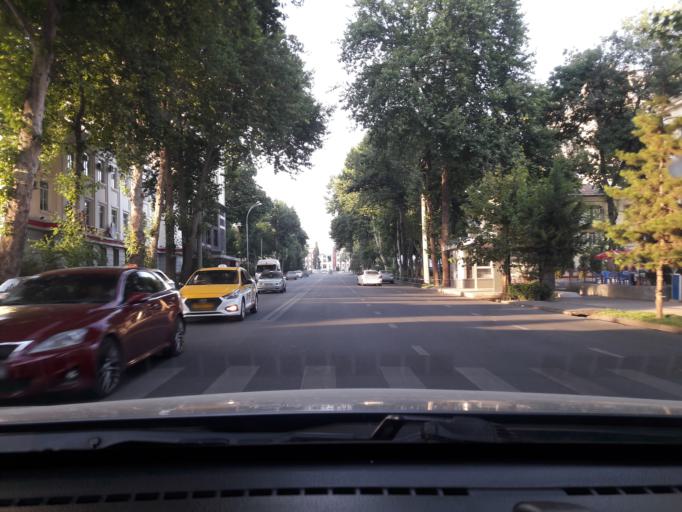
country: TJ
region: Dushanbe
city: Dushanbe
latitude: 38.5724
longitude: 68.7909
